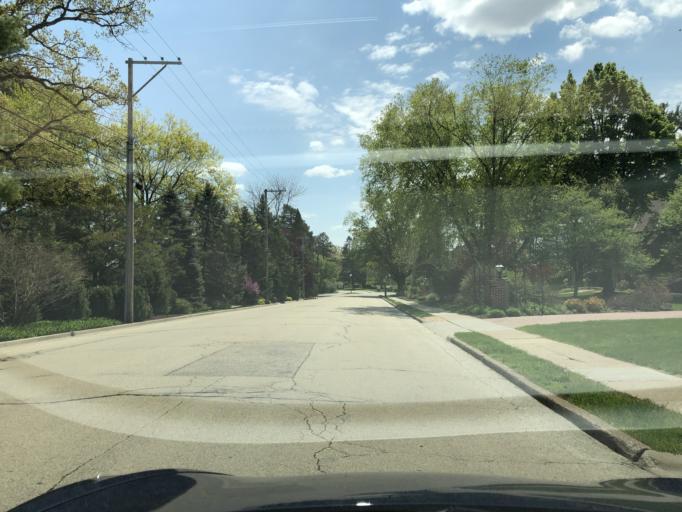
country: US
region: Illinois
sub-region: Jo Daviess County
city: East Dubuque
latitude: 42.4785
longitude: -90.6601
